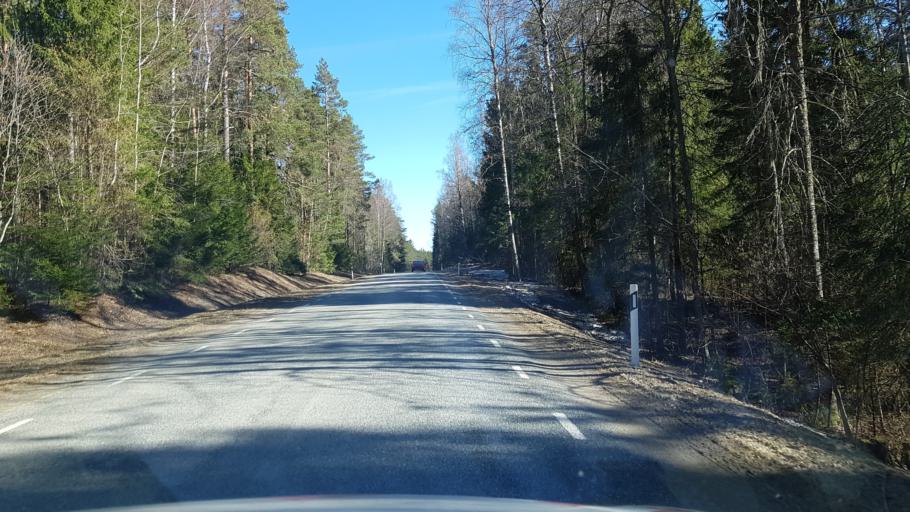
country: EE
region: Laeaene-Virumaa
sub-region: Vinni vald
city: Vinni
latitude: 59.2660
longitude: 26.6719
